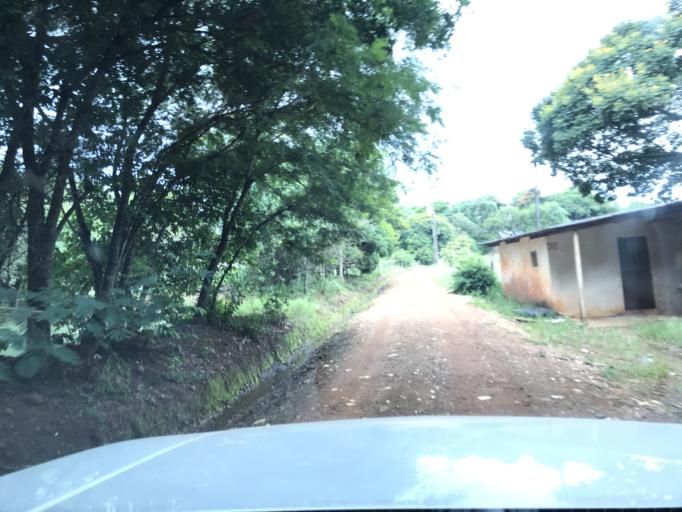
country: BR
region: Parana
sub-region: Palotina
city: Palotina
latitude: -24.2731
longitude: -53.7879
